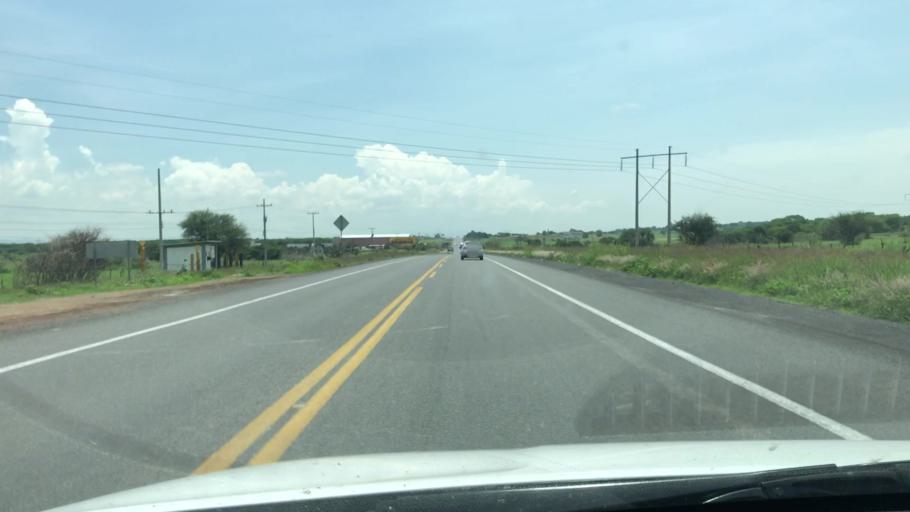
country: MX
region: Jalisco
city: Degollado
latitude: 20.3619
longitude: -102.1462
